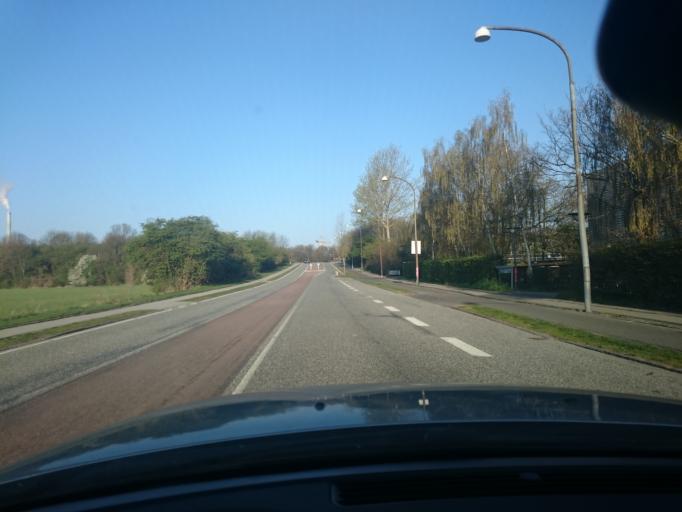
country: DK
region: Capital Region
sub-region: Lyngby-Tarbaek Kommune
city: Kongens Lyngby
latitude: 55.7877
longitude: 12.5325
